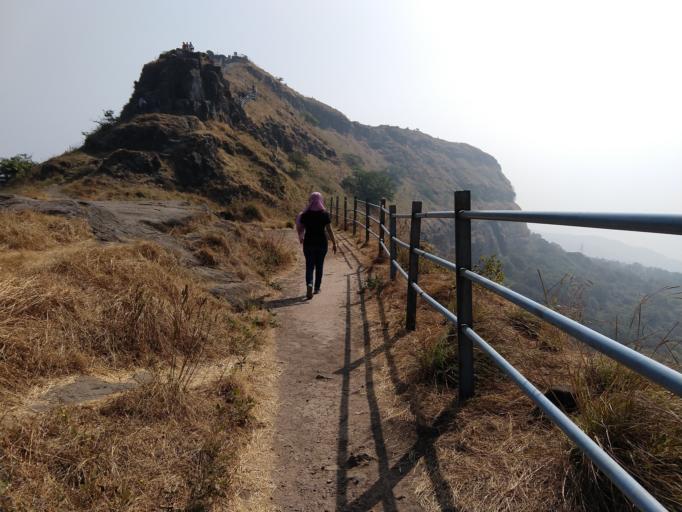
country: IN
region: Maharashtra
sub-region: Pune Division
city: Lonavla
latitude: 18.7120
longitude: 73.4725
